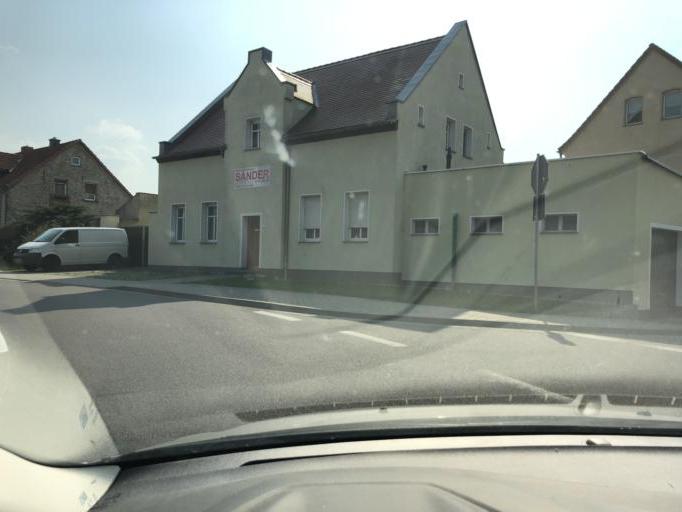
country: DE
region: Saxony-Anhalt
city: Grobers
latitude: 51.4449
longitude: 12.1120
